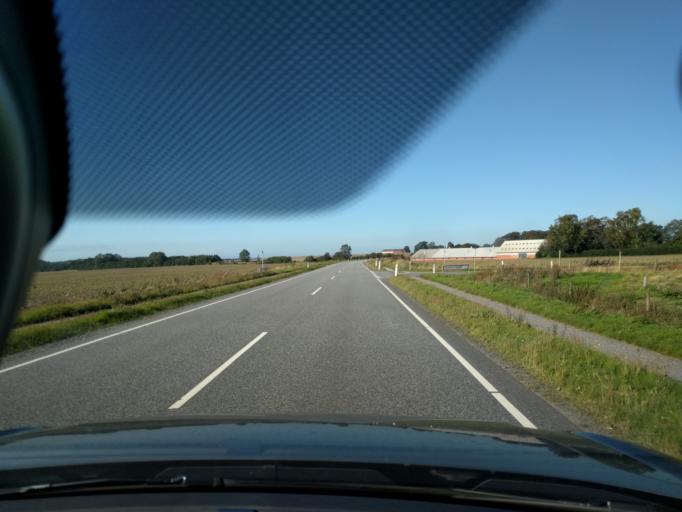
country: DK
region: North Denmark
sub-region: Vesthimmerland Kommune
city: Aars
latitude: 56.7451
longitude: 9.5923
